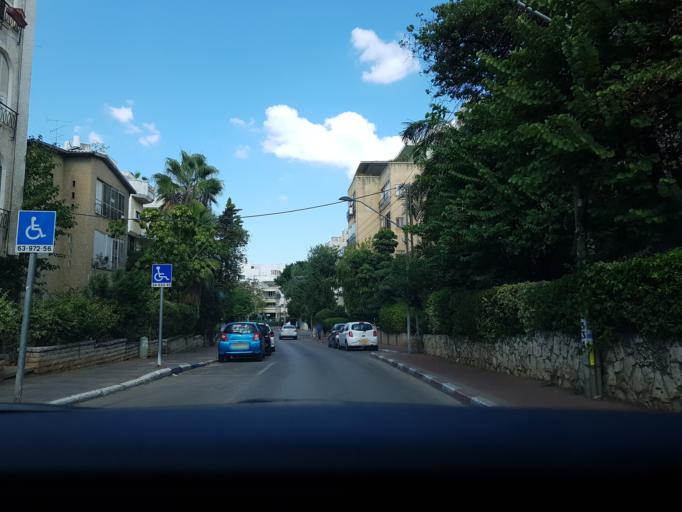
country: IL
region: Central District
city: Ness Ziona
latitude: 31.8997
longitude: 34.8068
